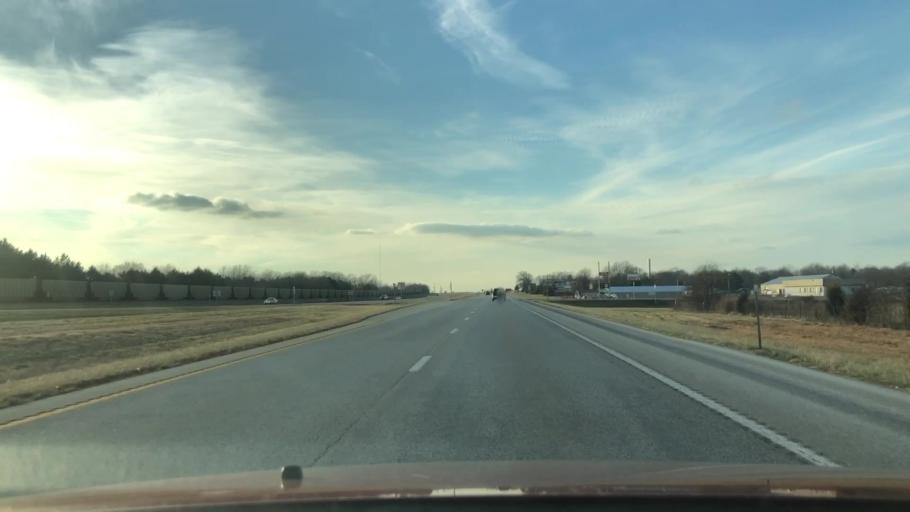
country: US
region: Missouri
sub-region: Webster County
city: Seymour
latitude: 37.1718
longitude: -92.8445
